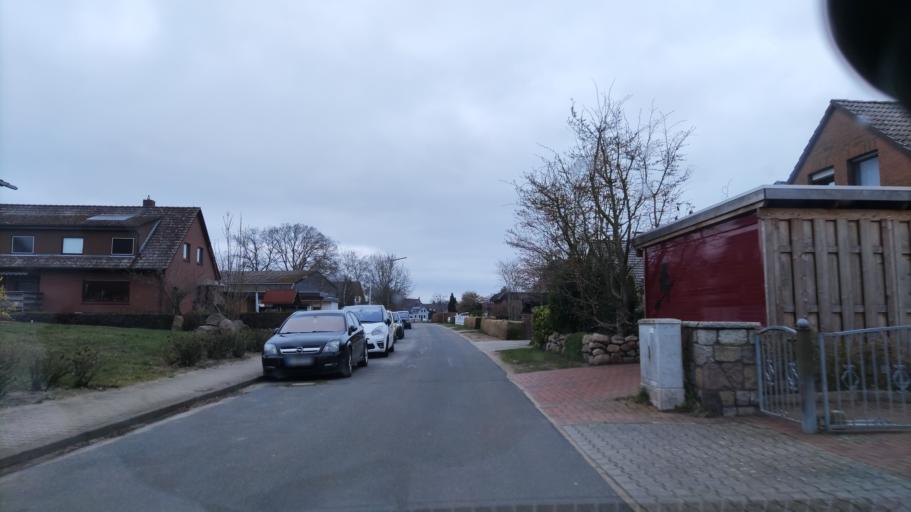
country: DE
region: Lower Saxony
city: Handorf
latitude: 53.3393
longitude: 10.3413
